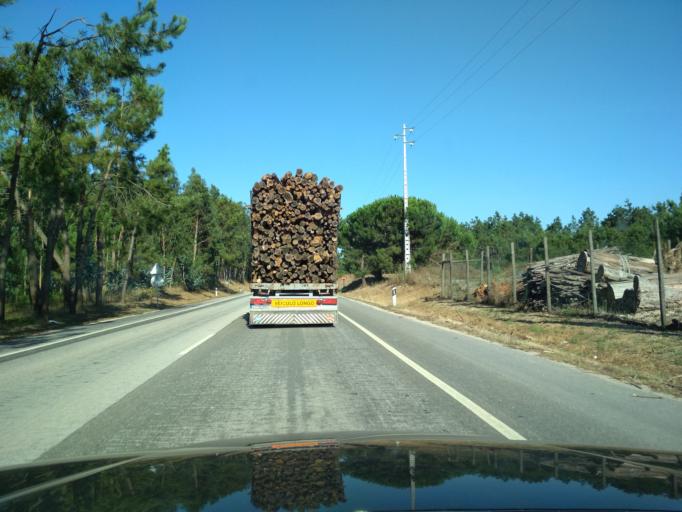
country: PT
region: Coimbra
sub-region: Figueira da Foz
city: Lavos
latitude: 40.0244
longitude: -8.8262
